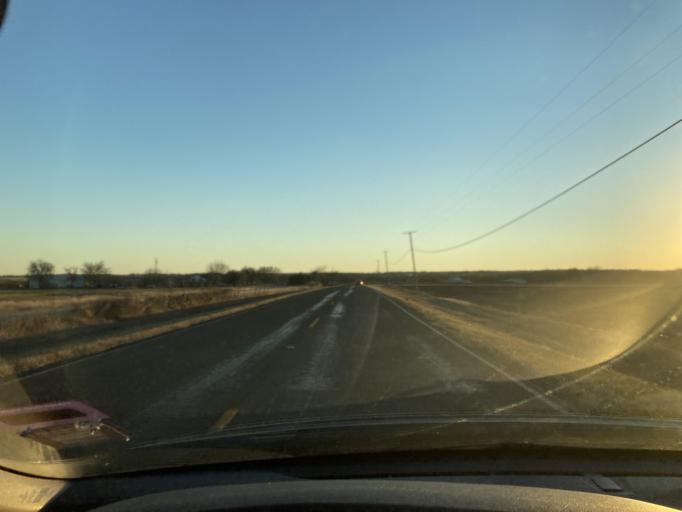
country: US
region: Texas
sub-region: Ellis County
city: Waxahachie
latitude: 32.3617
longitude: -96.8669
